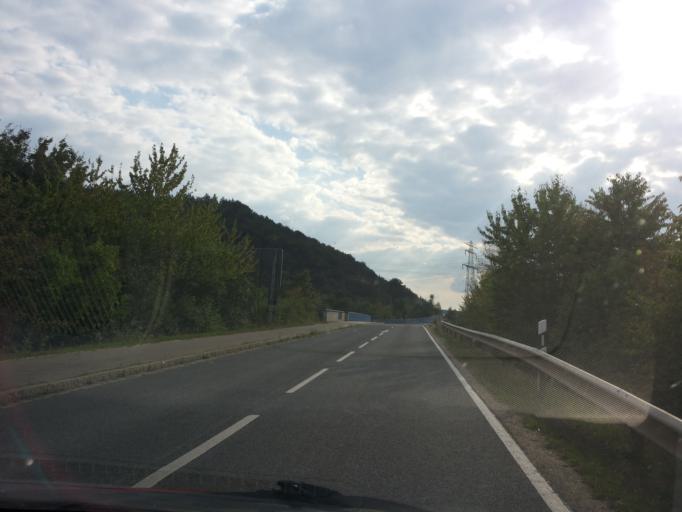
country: DE
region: Bavaria
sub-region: Upper Palatinate
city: Dietfurt
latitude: 49.0276
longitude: 11.5820
